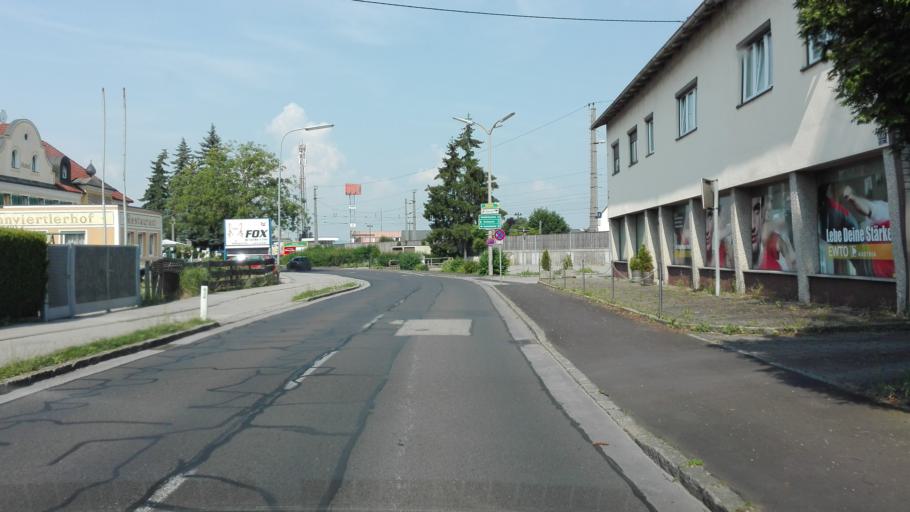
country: AT
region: Upper Austria
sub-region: Politischer Bezirk Linz-Land
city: Traun
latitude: 48.2265
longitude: 14.2538
